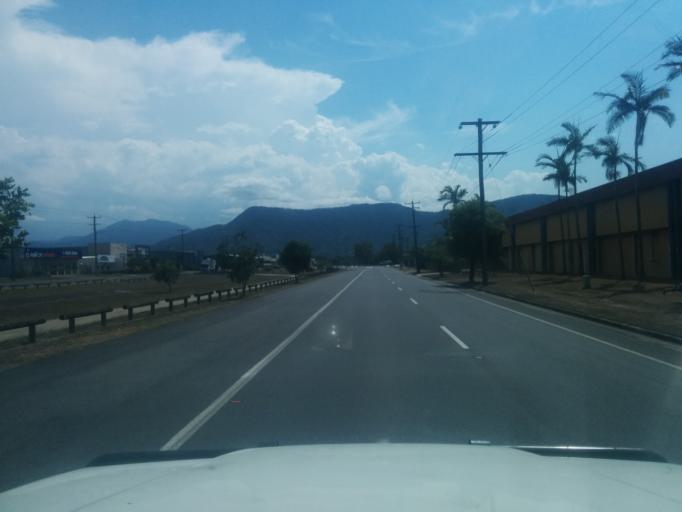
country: AU
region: Queensland
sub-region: Cairns
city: Woree
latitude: -16.9387
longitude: 145.7581
